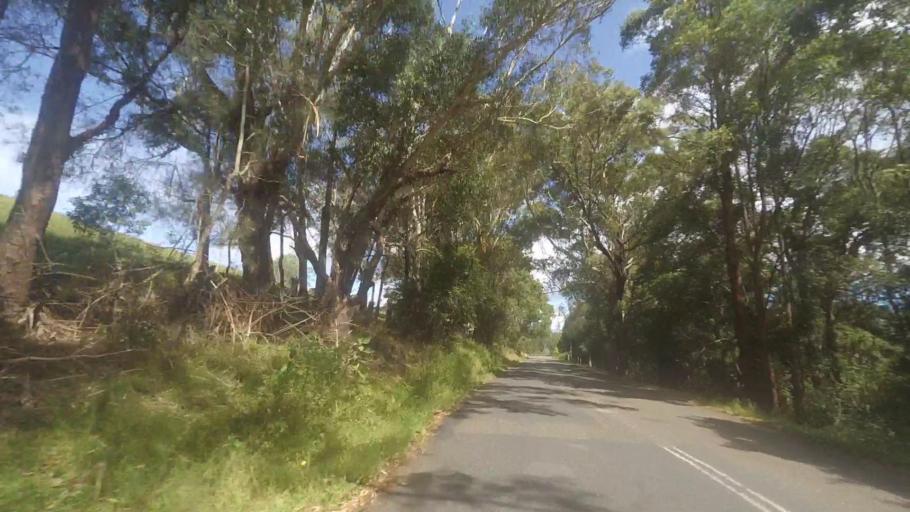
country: AU
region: New South Wales
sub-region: Great Lakes
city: Bulahdelah
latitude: -32.3923
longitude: 152.4368
